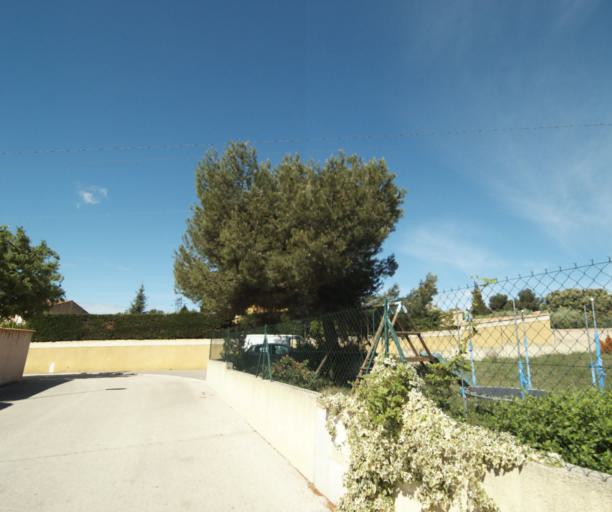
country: FR
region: Provence-Alpes-Cote d'Azur
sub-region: Departement des Bouches-du-Rhone
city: Rognac
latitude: 43.5096
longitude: 5.2124
